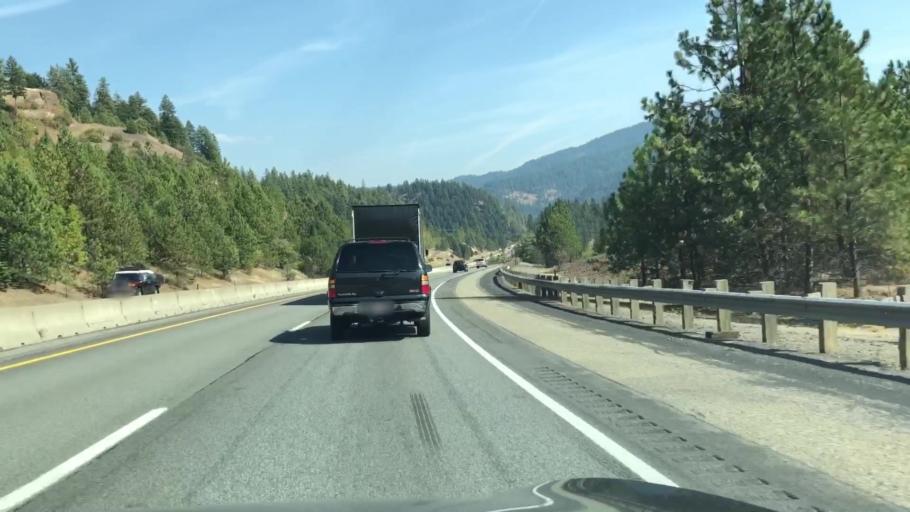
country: US
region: Idaho
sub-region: Kootenai County
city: Coeur d'Alene
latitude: 47.6313
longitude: -116.6927
